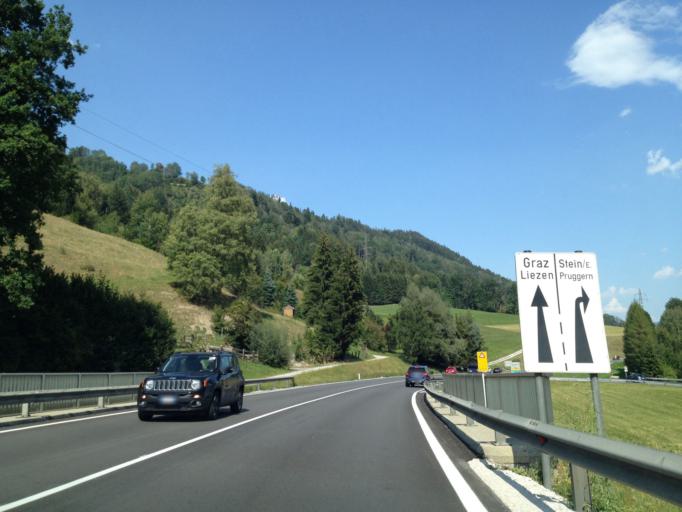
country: AT
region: Styria
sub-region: Politischer Bezirk Liezen
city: Pruggern
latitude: 47.4275
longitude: 13.8696
